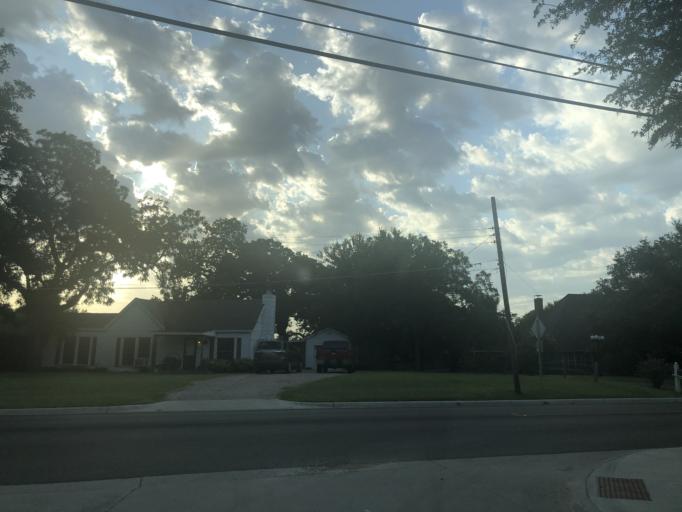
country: US
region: Texas
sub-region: Dallas County
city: Grand Prairie
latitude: 32.7634
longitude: -97.0127
